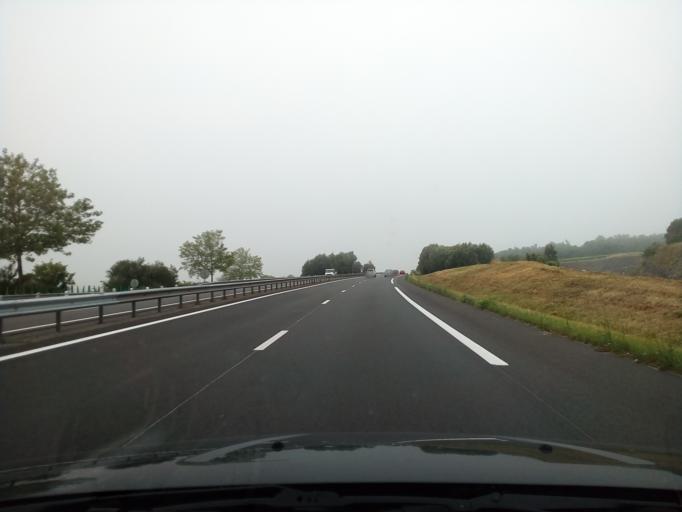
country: FR
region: Poitou-Charentes
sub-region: Departement de la Charente
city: Gensac-la-Pallue
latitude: 45.6641
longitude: -0.2292
